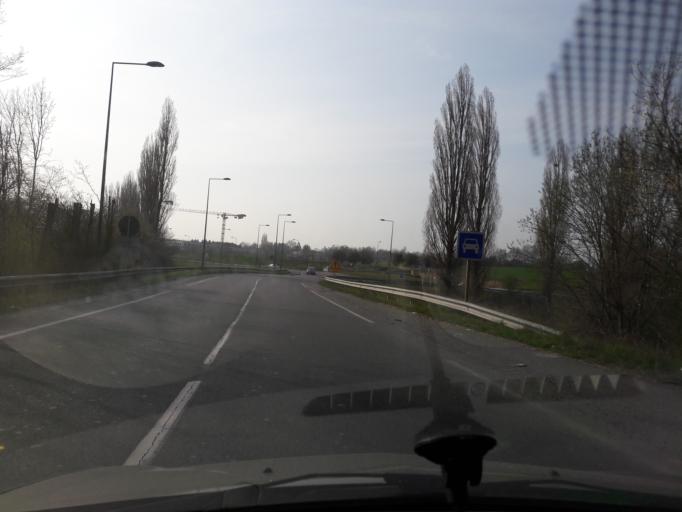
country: FR
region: Nord-Pas-de-Calais
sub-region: Departement du Nord
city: Rousies
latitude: 50.2792
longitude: 3.9969
